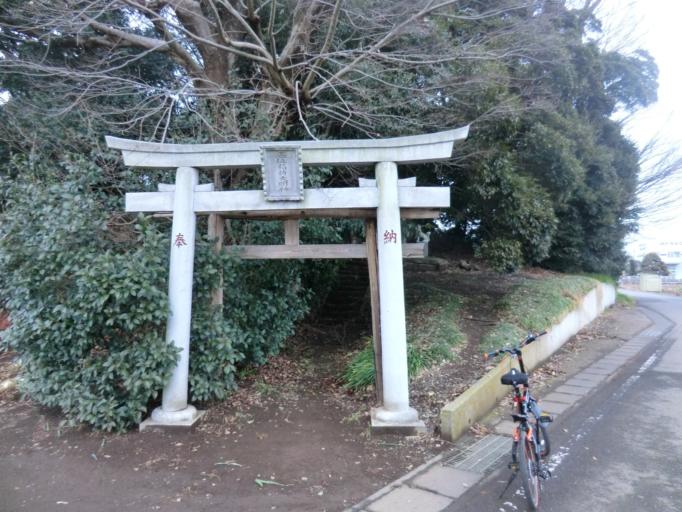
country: JP
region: Ibaraki
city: Naka
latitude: 36.0935
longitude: 140.1577
